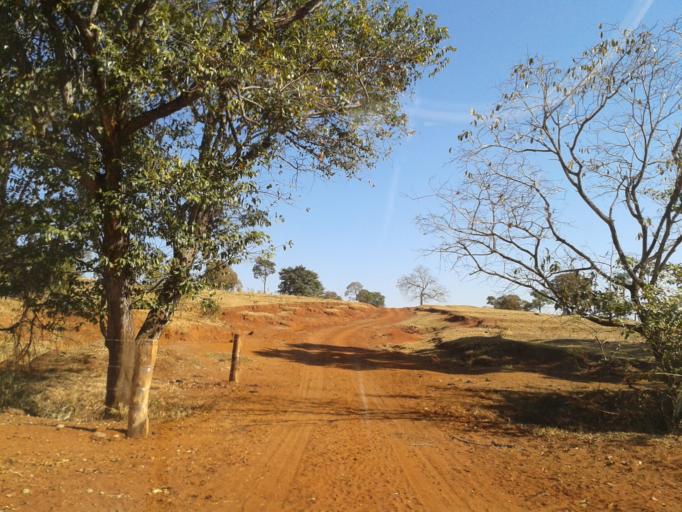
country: BR
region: Minas Gerais
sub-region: Santa Vitoria
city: Santa Vitoria
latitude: -19.0574
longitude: -49.9282
